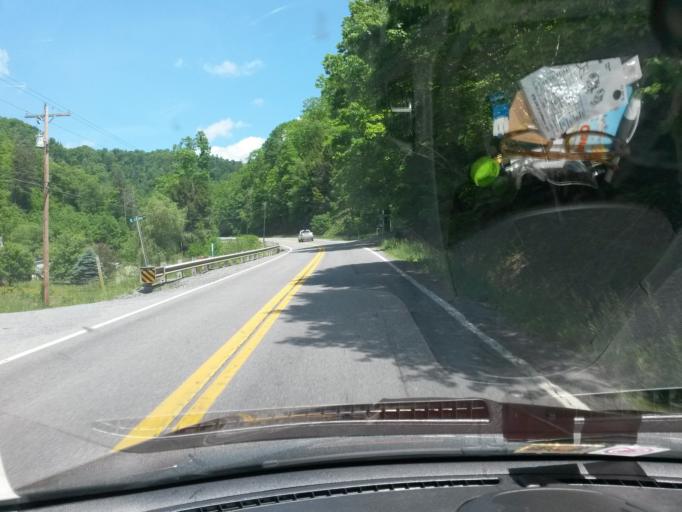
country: US
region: West Virginia
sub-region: McDowell County
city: Welch
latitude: 37.4767
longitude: -81.5437
